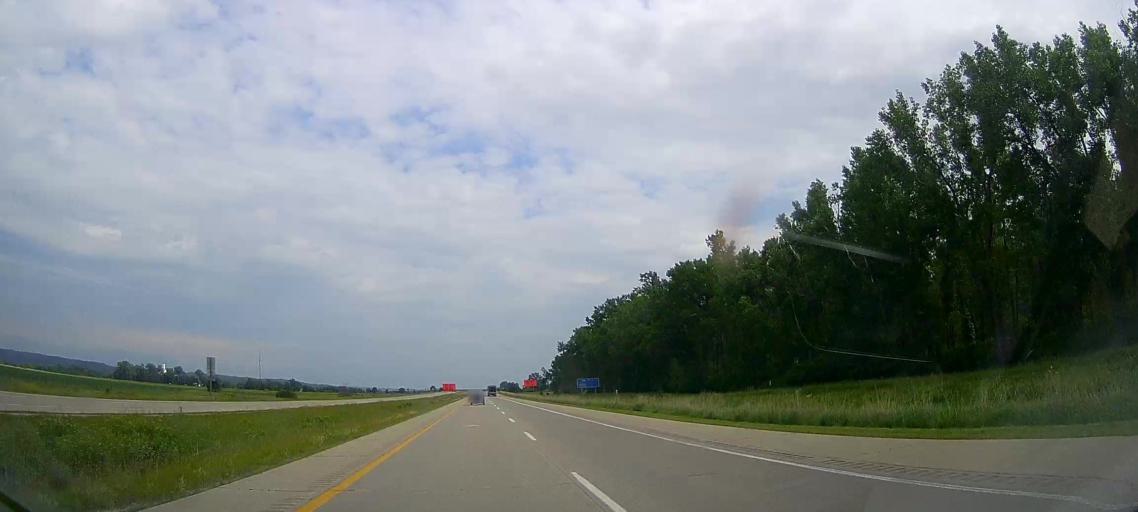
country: US
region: Nebraska
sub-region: Burt County
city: Tekamah
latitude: 41.8103
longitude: -96.0630
